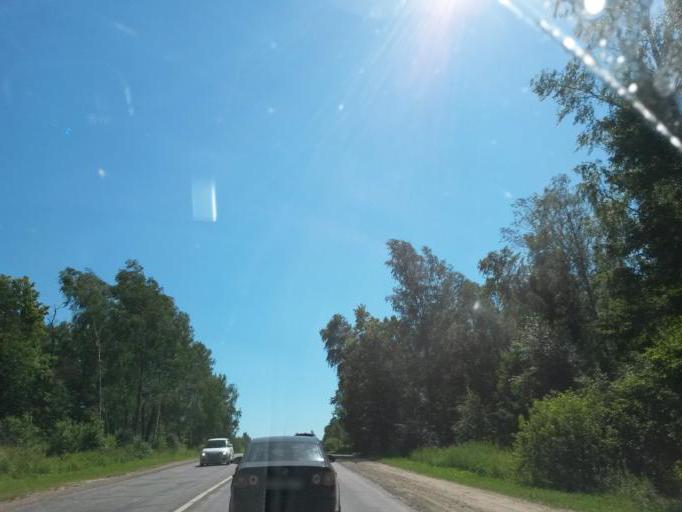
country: RU
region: Moskovskaya
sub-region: Chekhovskiy Rayon
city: Chekhov
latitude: 55.1071
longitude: 37.4462
